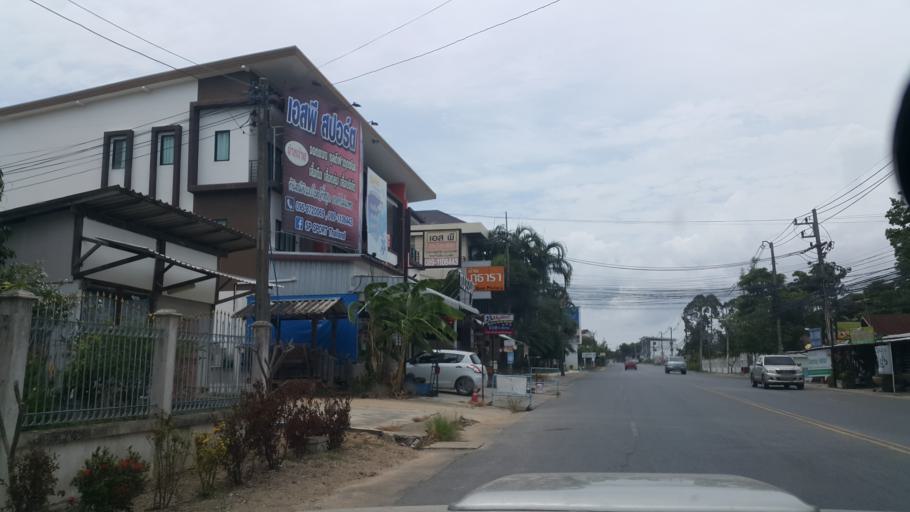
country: TH
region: Rayong
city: Ban Chang
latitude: 12.7133
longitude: 101.0491
